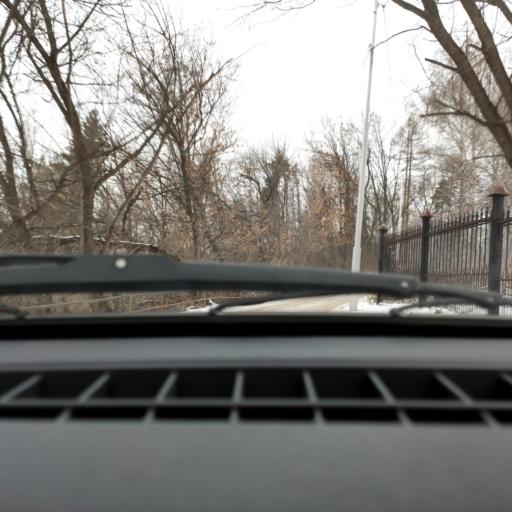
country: RU
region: Bashkortostan
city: Ufa
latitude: 54.8198
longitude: 56.0550
